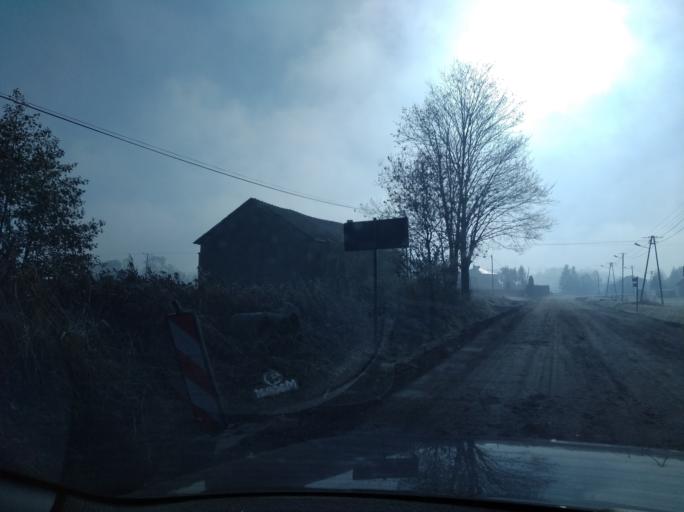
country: PL
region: Subcarpathian Voivodeship
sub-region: Powiat strzyzowski
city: Wisniowa
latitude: 49.8726
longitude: 21.7055
